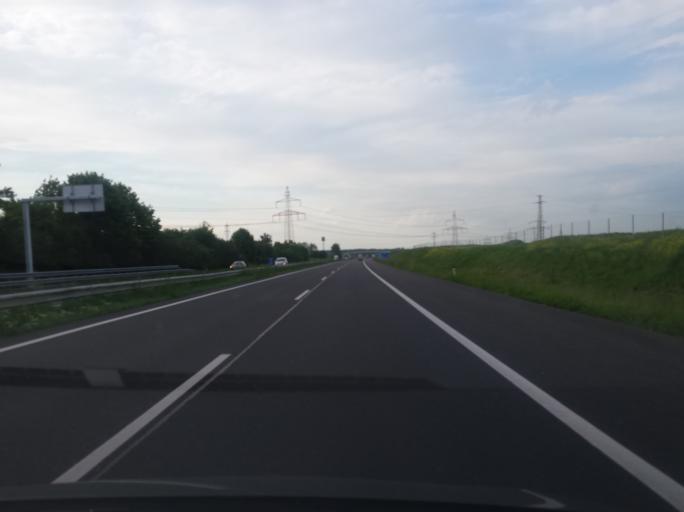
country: AT
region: Burgenland
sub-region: Eisenstadt-Umgebung
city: Hornstein
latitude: 47.8711
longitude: 16.4176
